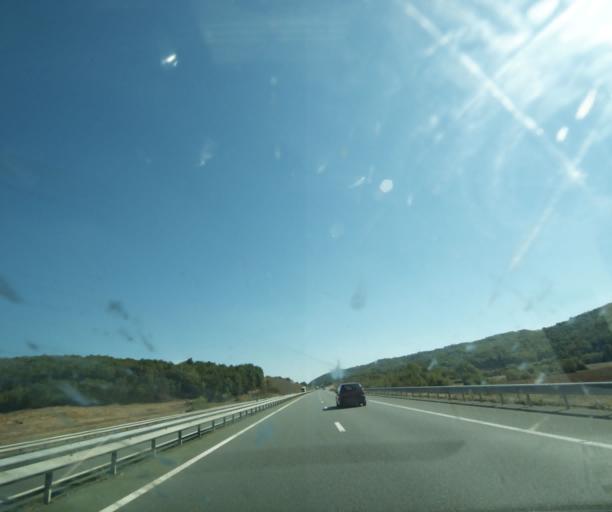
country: FR
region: Midi-Pyrenees
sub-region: Departement du Lot
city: Souillac
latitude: 44.8200
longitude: 1.4981
